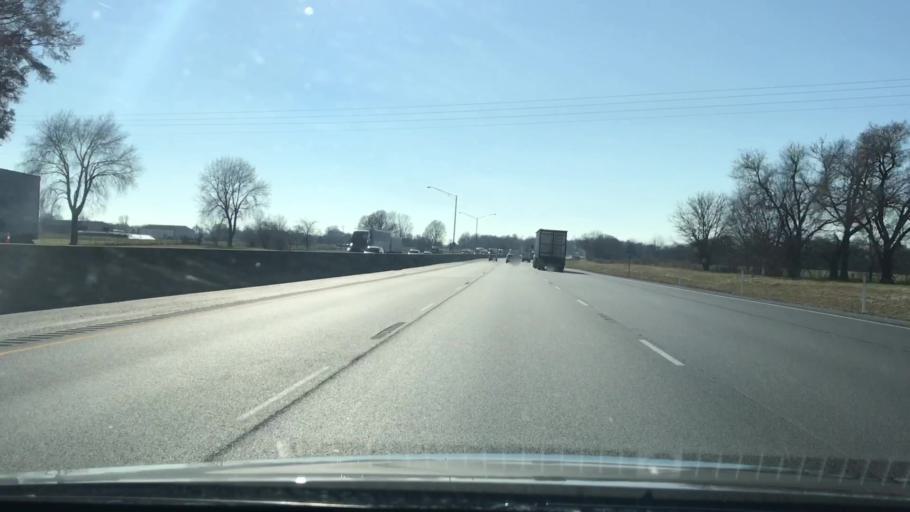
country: US
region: Kentucky
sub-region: Edmonson County
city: Brownsville
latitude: 37.0275
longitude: -86.2433
